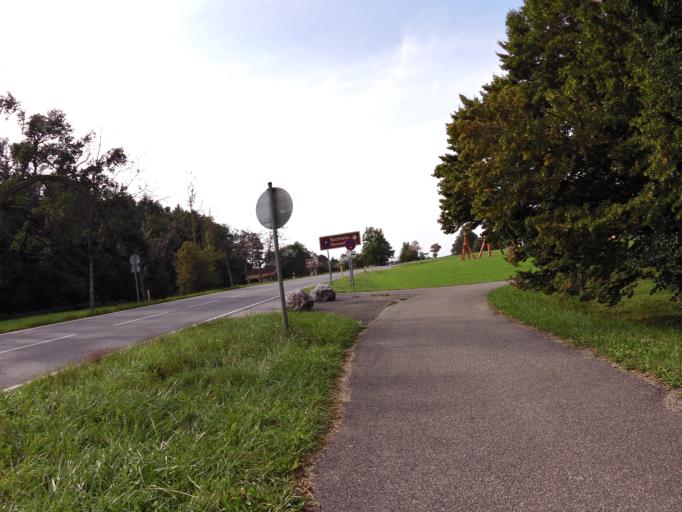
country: DE
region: Bavaria
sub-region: Upper Bavaria
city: Bernried
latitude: 47.8723
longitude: 11.2845
